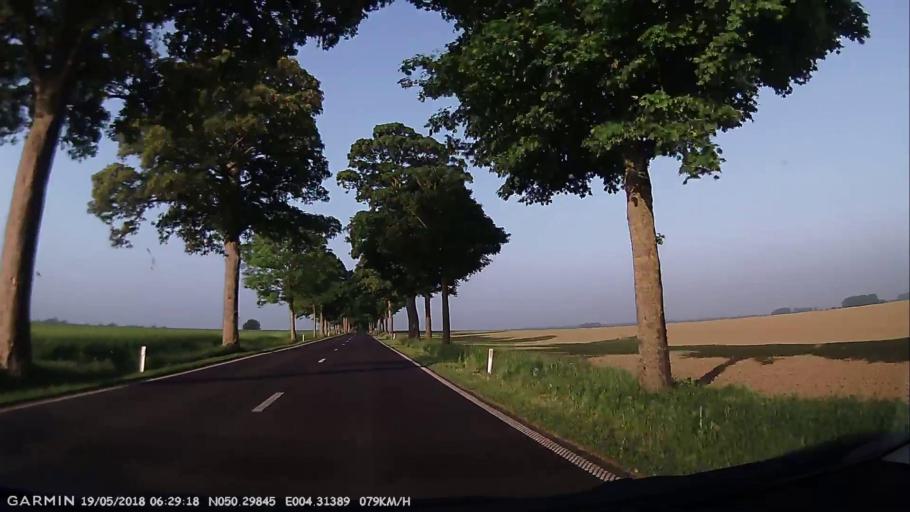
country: BE
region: Wallonia
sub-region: Province du Hainaut
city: Thuin
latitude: 50.2983
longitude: 4.3137
